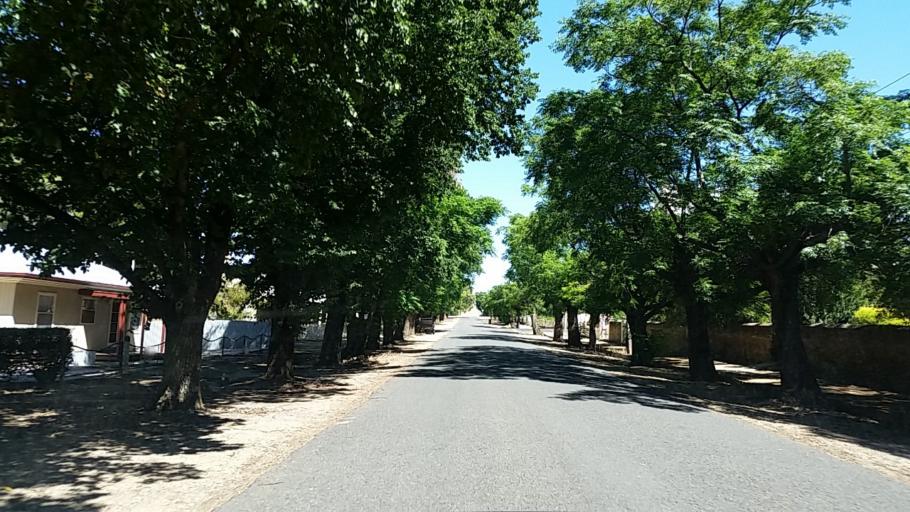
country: AU
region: South Australia
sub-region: Clare and Gilbert Valleys
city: Clare
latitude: -33.6841
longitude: 138.9397
